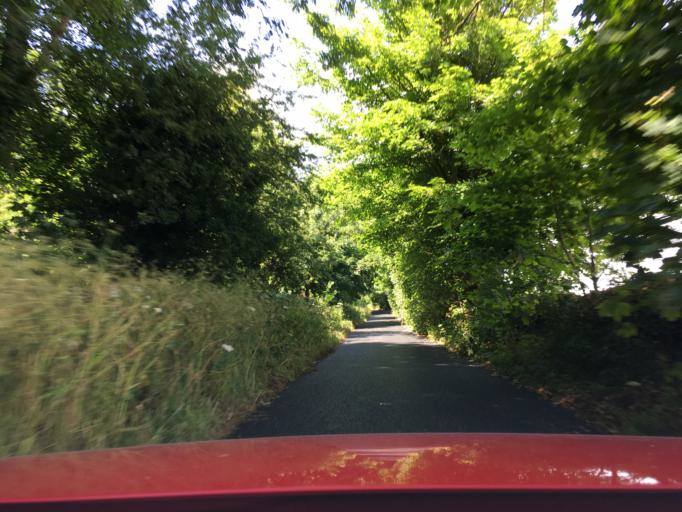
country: GB
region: England
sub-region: Gloucestershire
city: Tetbury
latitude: 51.6516
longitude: -2.1816
